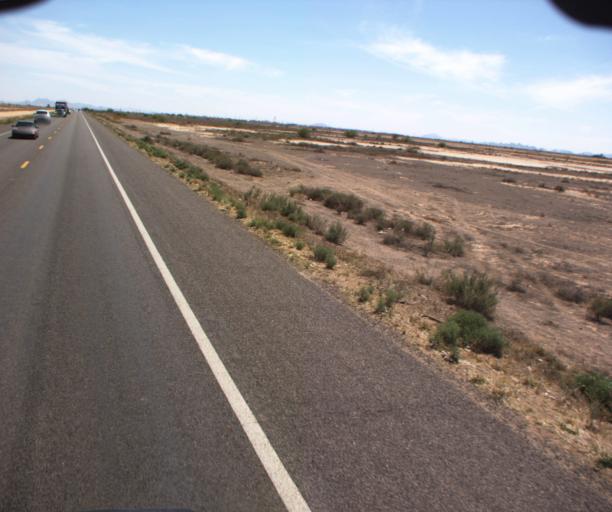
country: US
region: Arizona
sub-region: Pinal County
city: Eloy
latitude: 32.8350
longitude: -111.5153
